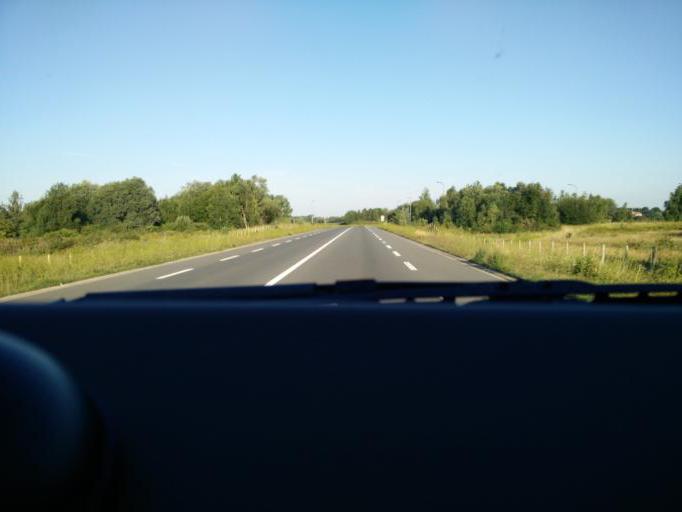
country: FR
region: Nord-Pas-de-Calais
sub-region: Departement du Nord
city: La Bassee
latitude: 50.5218
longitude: 2.8131
